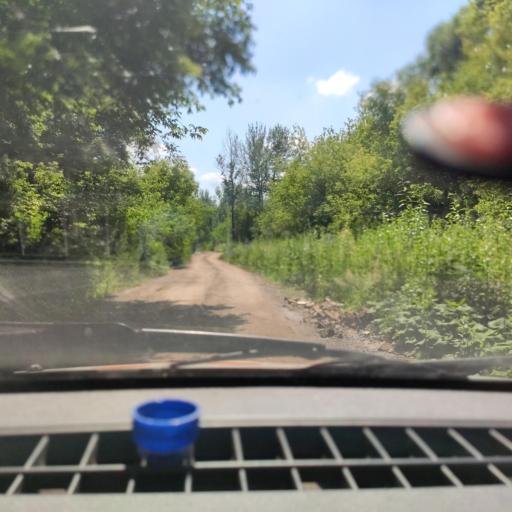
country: RU
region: Bashkortostan
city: Ufa
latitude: 54.6822
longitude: 55.9527
